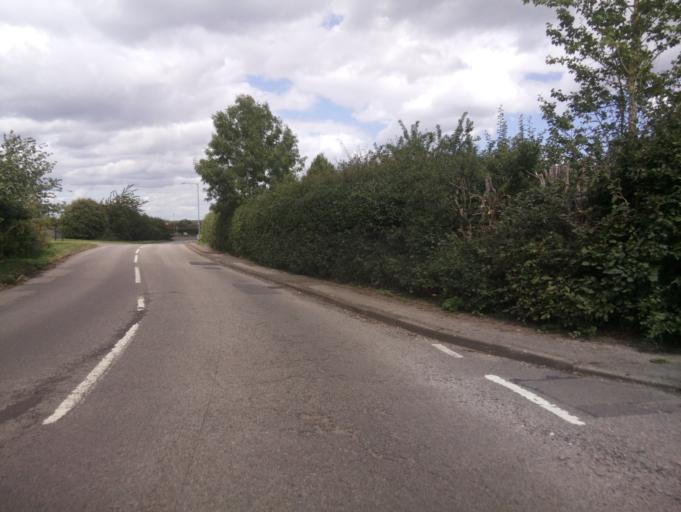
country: GB
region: England
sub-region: Nottinghamshire
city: Cotgrave
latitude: 52.8920
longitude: -1.0854
